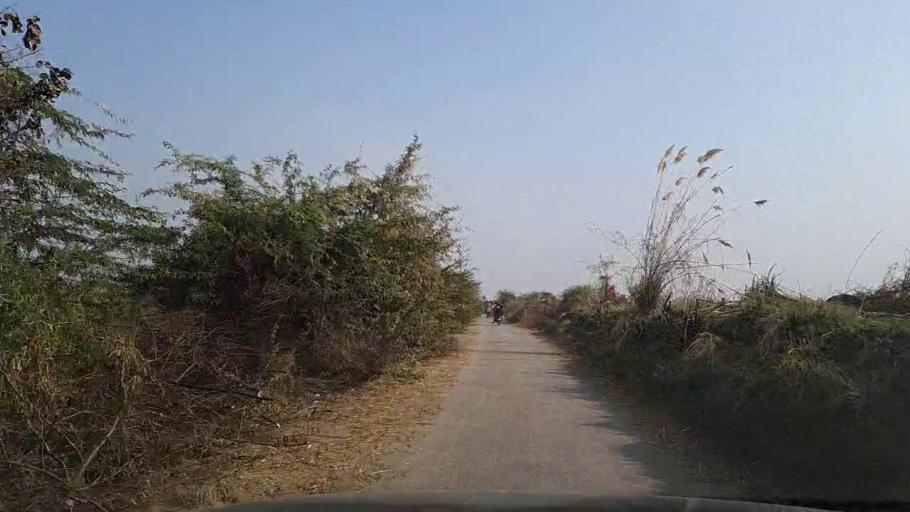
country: PK
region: Sindh
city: Thatta
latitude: 24.6495
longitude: 67.9250
